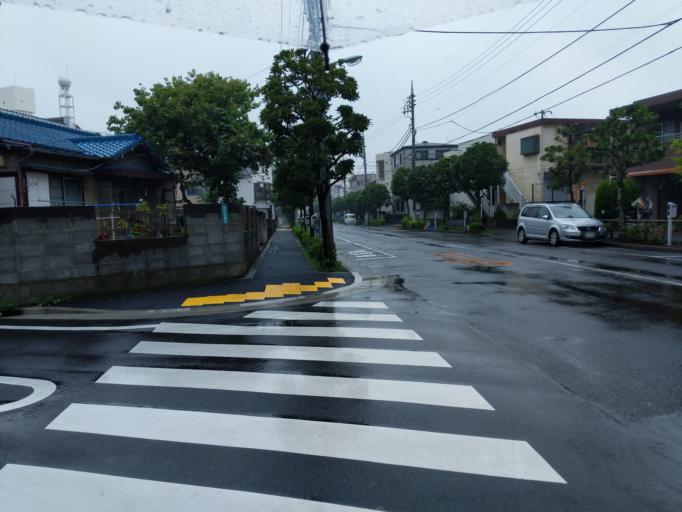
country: JP
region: Tokyo
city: Urayasu
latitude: 35.6617
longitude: 139.8670
